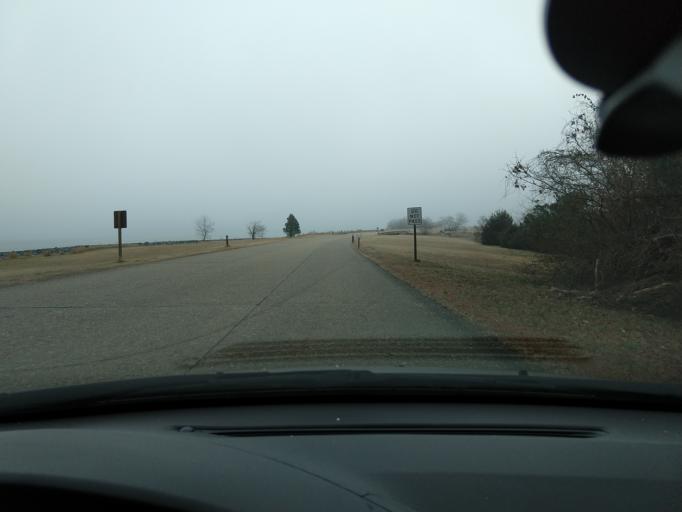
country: US
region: Virginia
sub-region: York County
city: Yorktown
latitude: 37.2694
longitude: -76.5593
